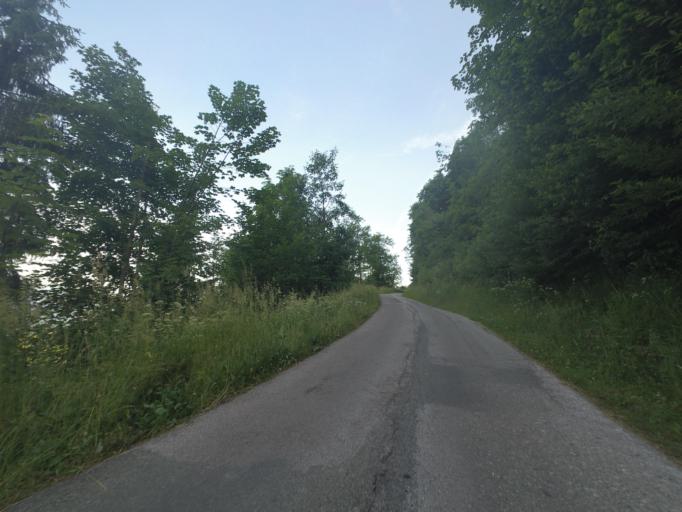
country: AT
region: Salzburg
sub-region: Politischer Bezirk Sankt Johann im Pongau
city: Muhlbach am Hochkonig
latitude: 47.3461
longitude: 13.1235
